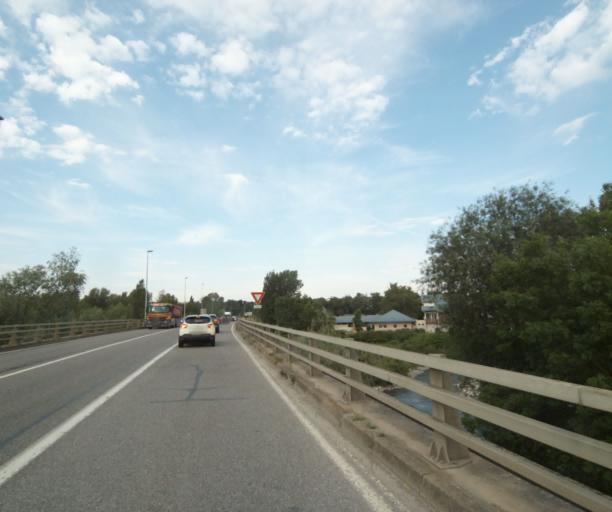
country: FR
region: Rhone-Alpes
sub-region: Departement de la Haute-Savoie
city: Marin
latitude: 46.3806
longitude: 6.5084
